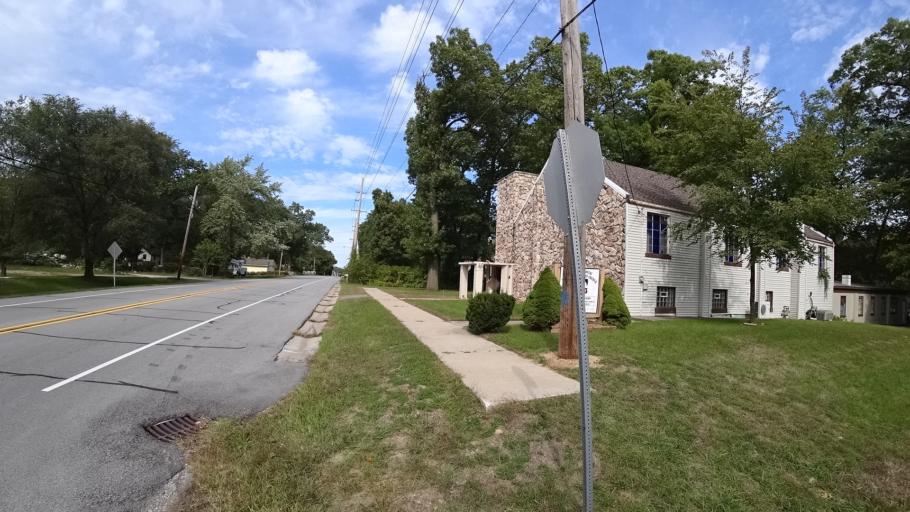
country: US
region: Indiana
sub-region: LaPorte County
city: Long Beach
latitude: 41.7286
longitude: -86.8554
